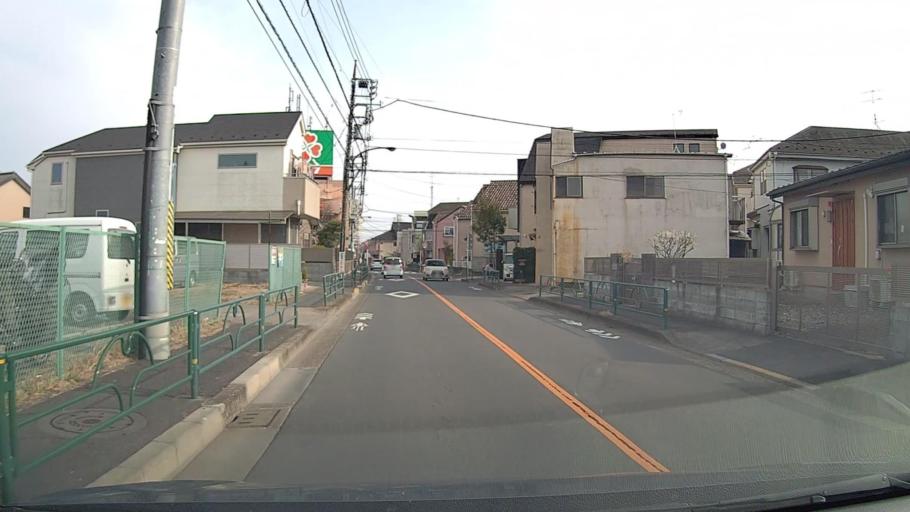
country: JP
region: Tokyo
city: Nishi-Tokyo-shi
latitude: 35.7571
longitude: 139.5784
